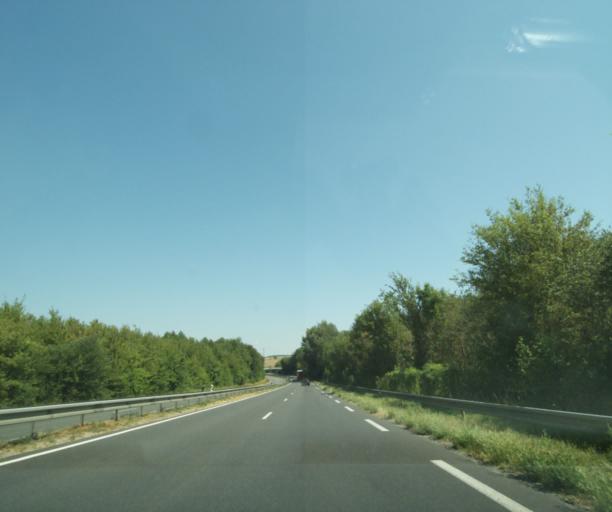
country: FR
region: Champagne-Ardenne
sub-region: Departement de la Marne
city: Vitry-le-Francois
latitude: 48.8272
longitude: 4.5376
